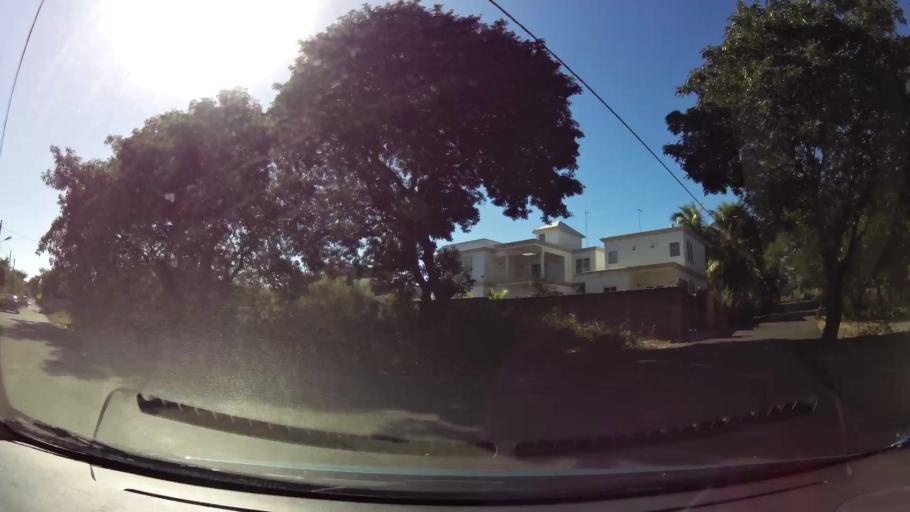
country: MU
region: Black River
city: Flic en Flac
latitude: -20.2670
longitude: 57.3757
